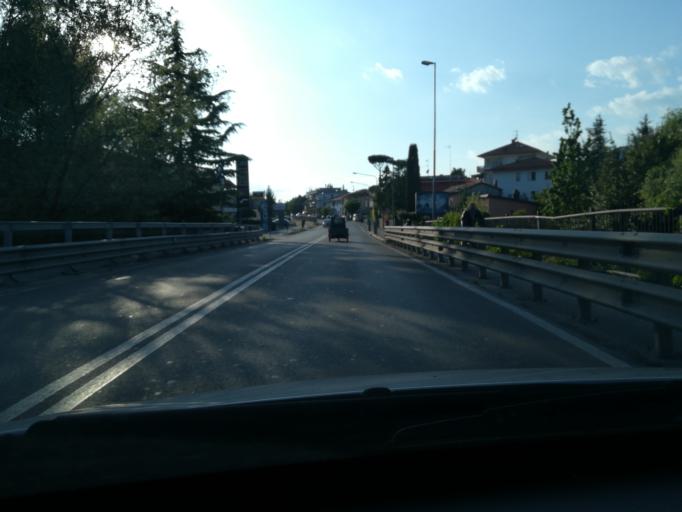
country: IT
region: Emilia-Romagna
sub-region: Provincia di Rimini
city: Riccione
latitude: 44.0002
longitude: 12.6430
